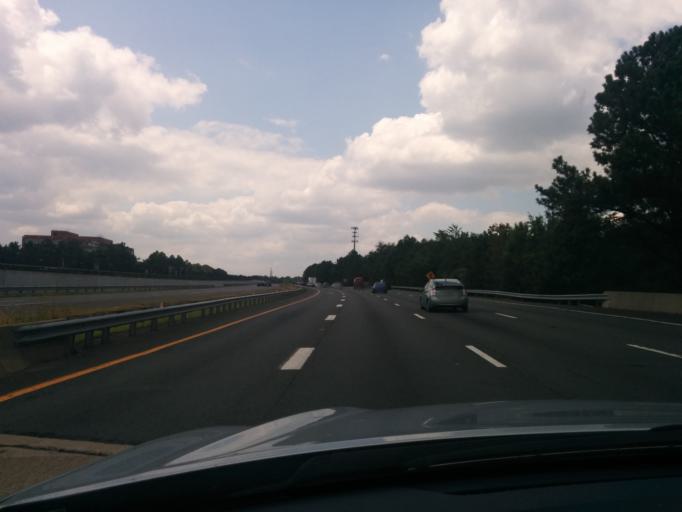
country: US
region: Virginia
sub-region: Fairfax County
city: Wolf Trap
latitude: 38.9481
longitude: -77.3119
